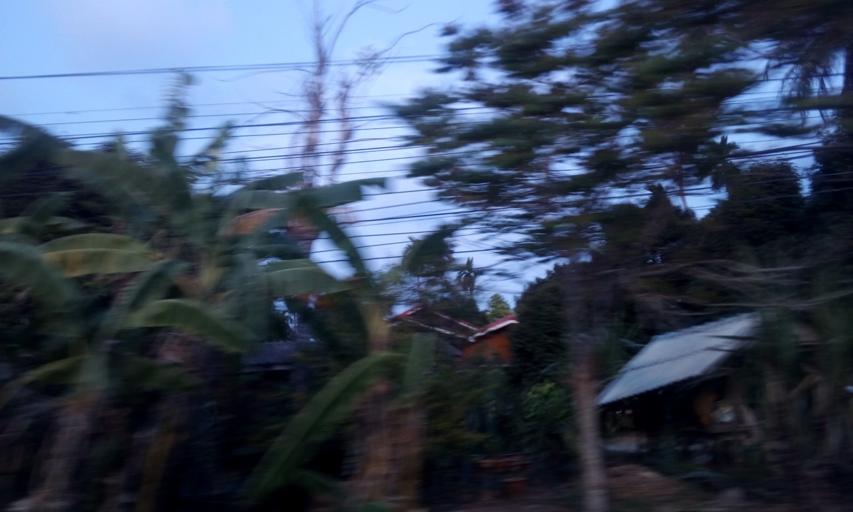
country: TH
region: Trat
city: Laem Ngop
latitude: 12.2445
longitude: 102.2941
